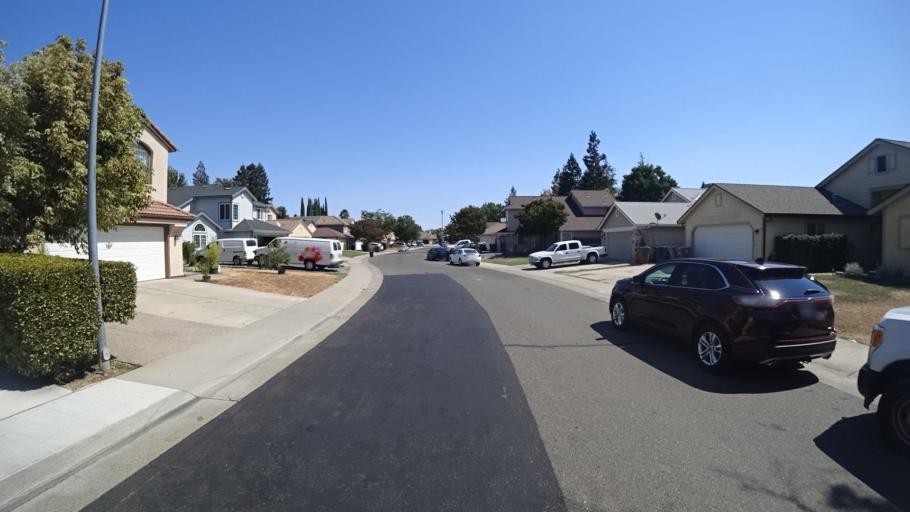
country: US
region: California
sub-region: Sacramento County
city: Laguna
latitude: 38.4156
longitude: -121.4161
